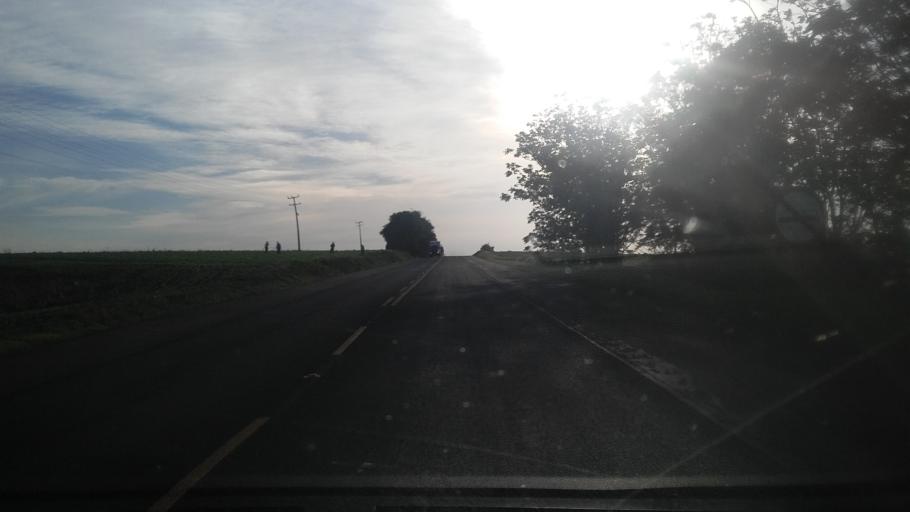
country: BR
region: Parana
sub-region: Bandeirantes
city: Bandeirantes
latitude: -23.1477
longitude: -50.5501
